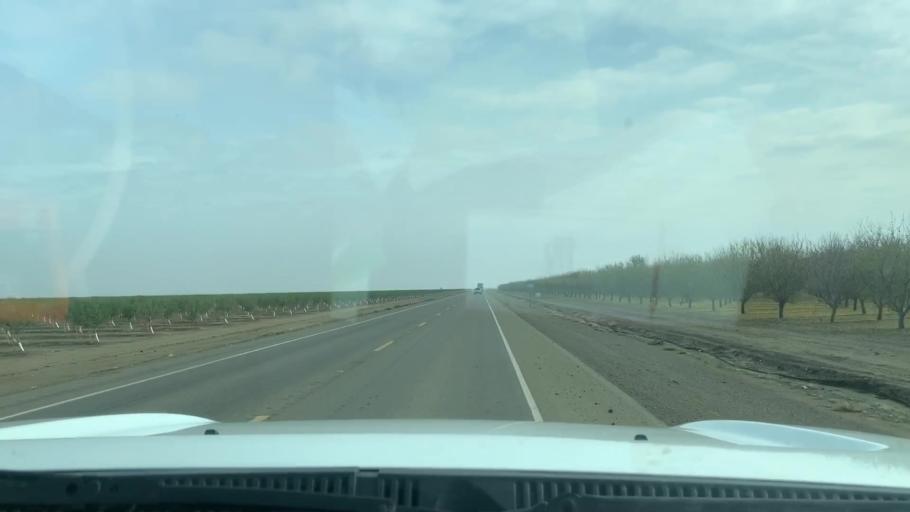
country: US
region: California
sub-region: Fresno County
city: Huron
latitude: 36.2554
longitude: -120.0121
